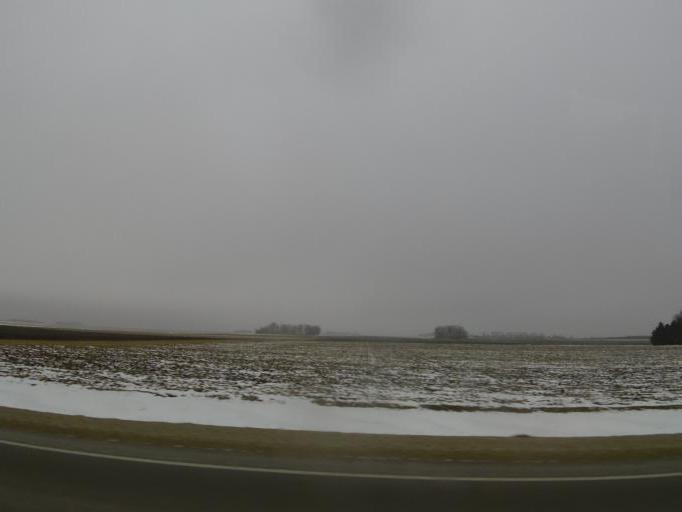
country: US
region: Minnesota
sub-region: Mower County
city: Grand Meadow
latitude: 43.7105
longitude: -92.5124
